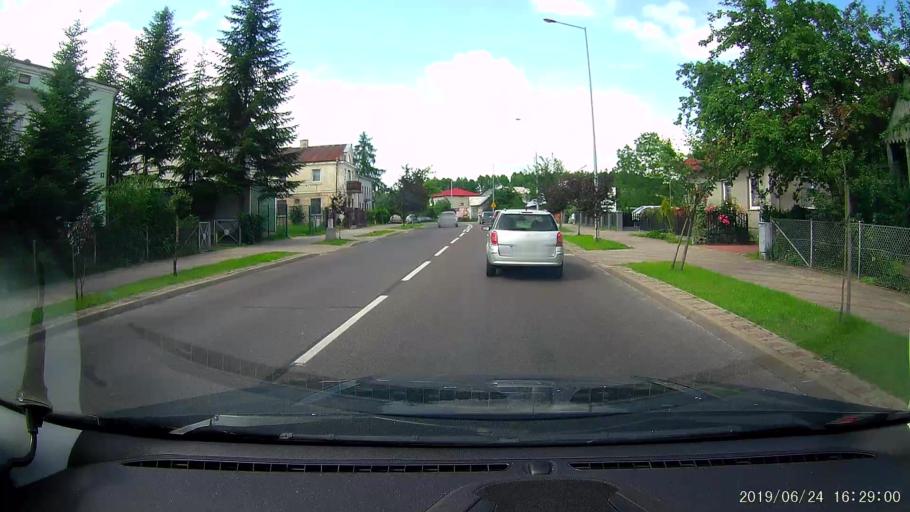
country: PL
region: Lublin Voivodeship
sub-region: Powiat tomaszowski
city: Tomaszow Lubelski
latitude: 50.4568
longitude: 23.4211
